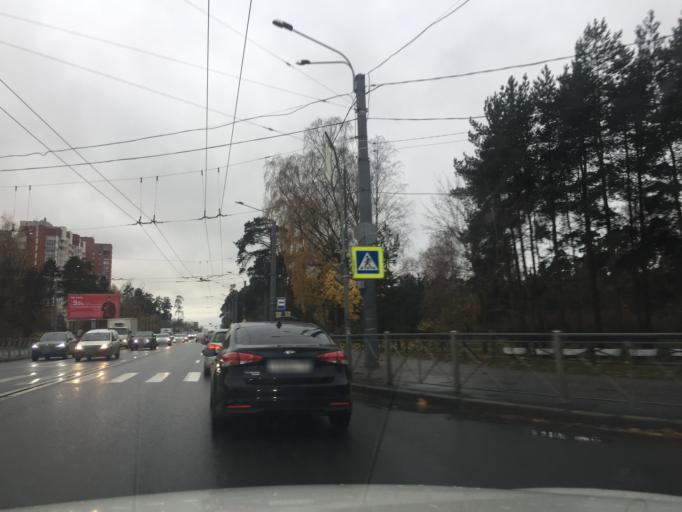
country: RU
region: St.-Petersburg
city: Sosnovka
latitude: 60.0133
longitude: 30.3535
